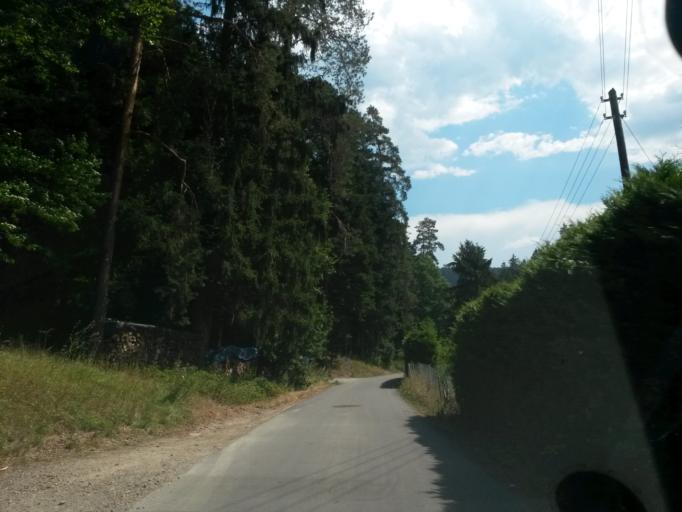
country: DE
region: Baden-Wuerttemberg
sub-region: Karlsruhe Region
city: Hofen an der Enz
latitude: 48.7615
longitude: 8.5935
